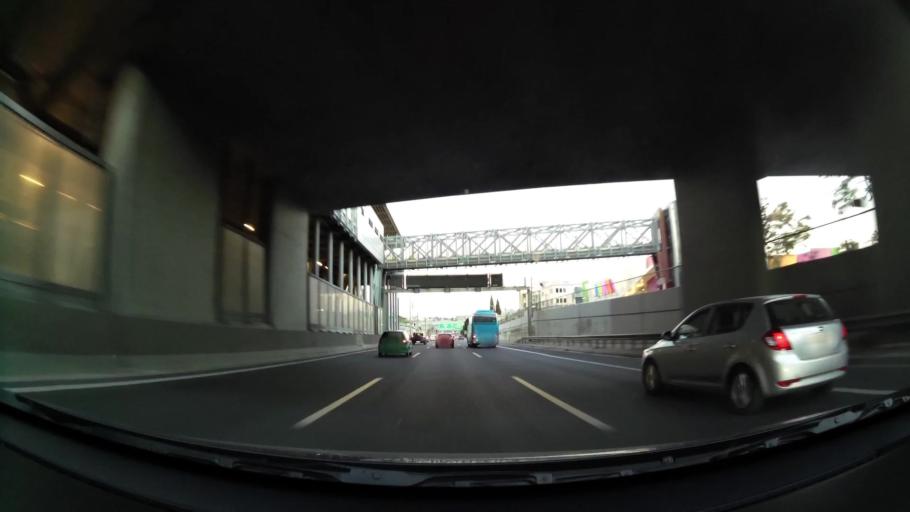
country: GR
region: Attica
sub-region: Nomarchia Athinas
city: Marousi
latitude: 38.0448
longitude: 23.7935
